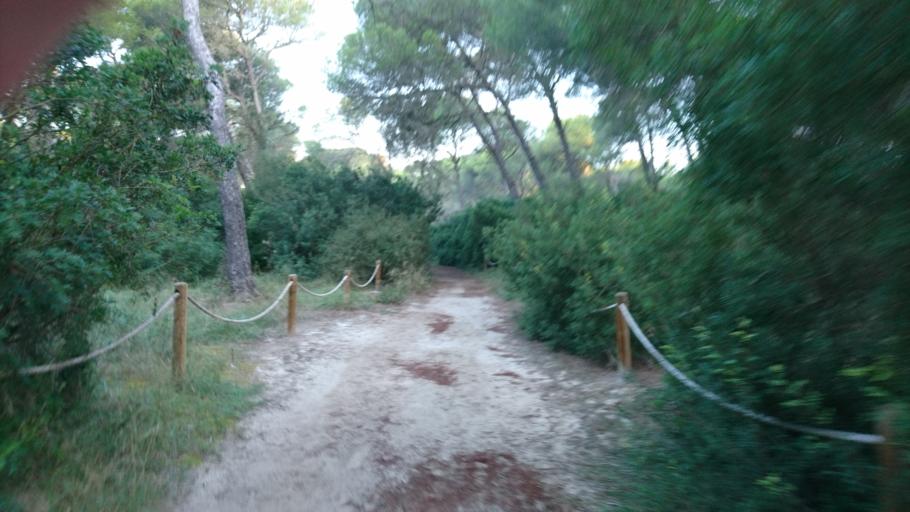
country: ES
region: Balearic Islands
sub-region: Illes Balears
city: Port d'Alcudia
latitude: 39.7819
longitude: 3.1323
